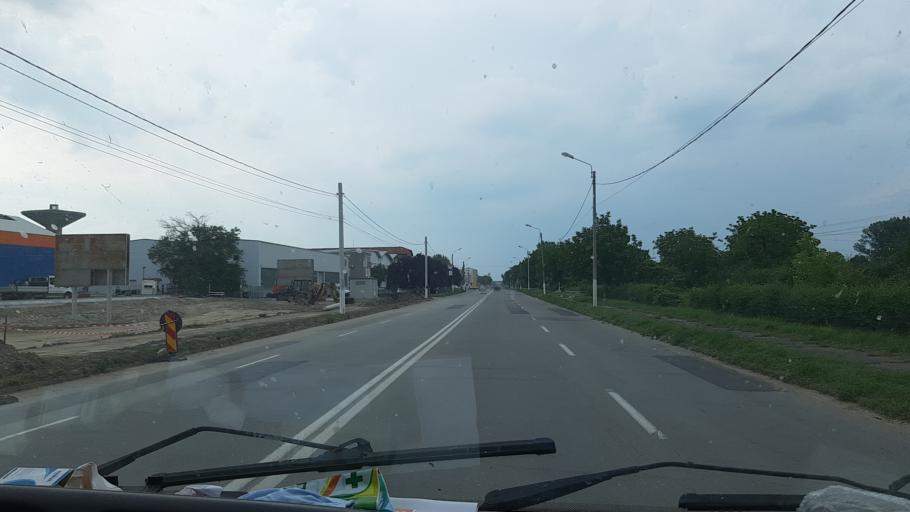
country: RO
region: Timis
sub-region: Municipiul Lugoj
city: Lugoj
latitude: 45.7039
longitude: 21.8912
